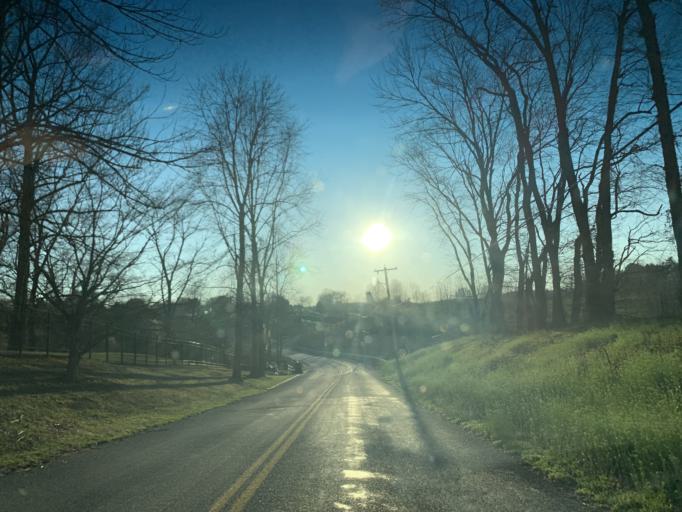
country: US
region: Maryland
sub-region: Harford County
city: South Bel Air
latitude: 39.5954
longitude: -76.2723
